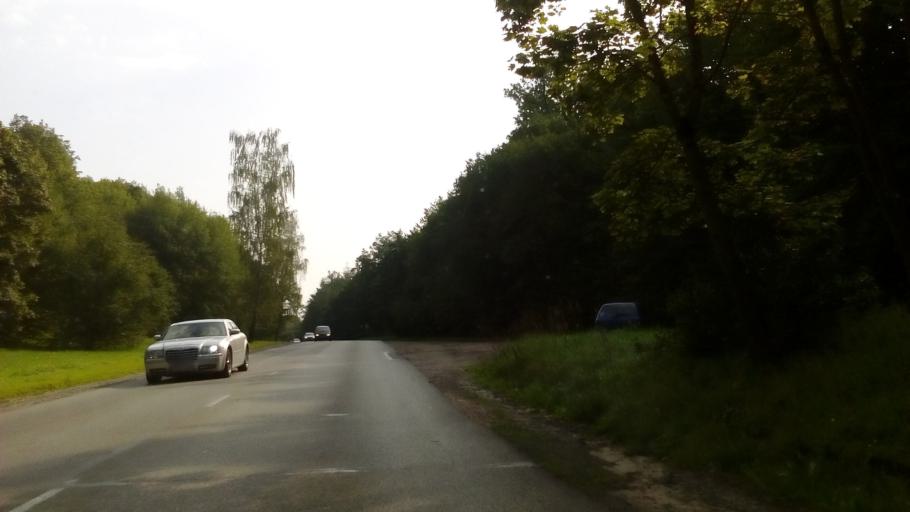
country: LT
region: Alytaus apskritis
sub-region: Alytus
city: Alytus
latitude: 54.3868
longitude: 24.0066
